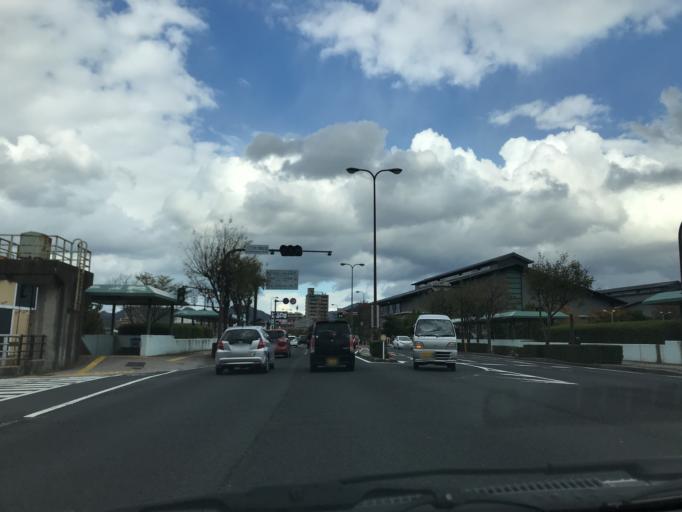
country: JP
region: Shimane
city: Matsue-shi
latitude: 35.4692
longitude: 133.0653
